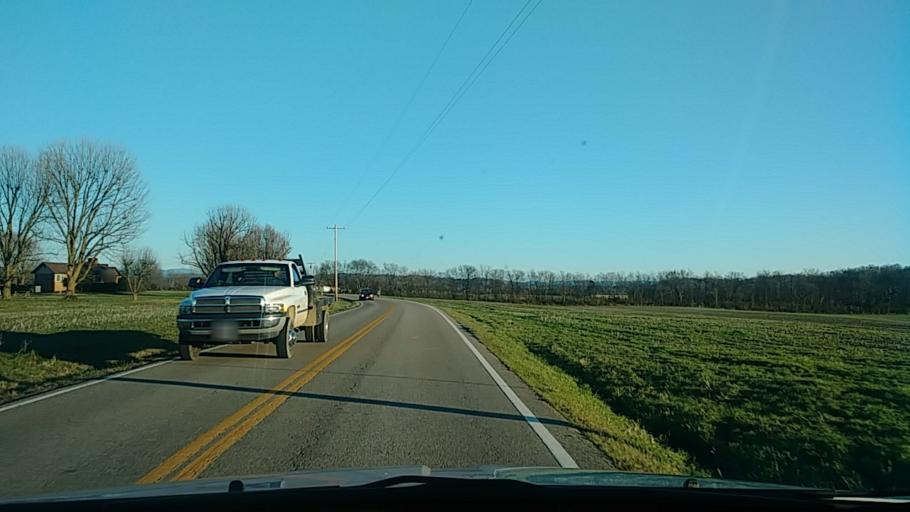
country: US
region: Tennessee
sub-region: Jefferson County
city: White Pine
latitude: 36.1521
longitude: -83.1573
